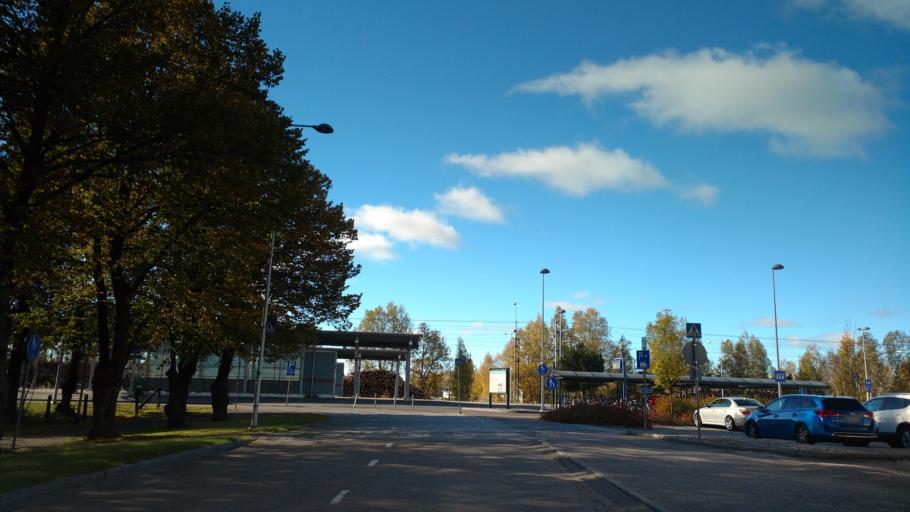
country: FI
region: Varsinais-Suomi
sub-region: Salo
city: Salo
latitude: 60.3860
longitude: 23.1214
